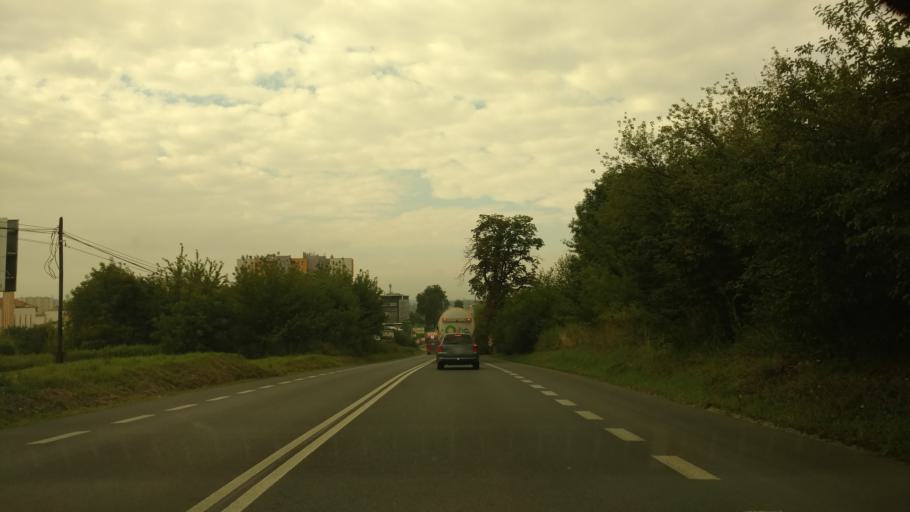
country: PL
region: Lesser Poland Voivodeship
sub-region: Powiat krakowski
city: Zielonki
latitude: 50.1039
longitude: 19.9640
